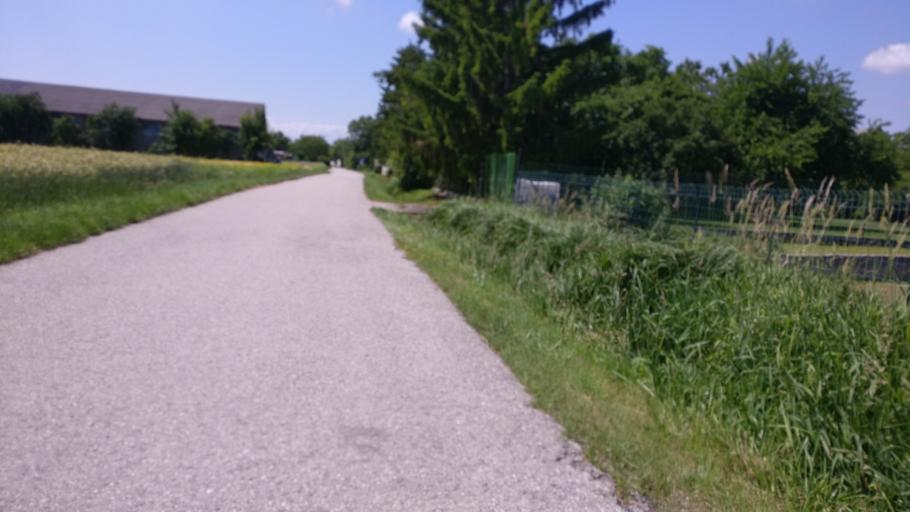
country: AT
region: Lower Austria
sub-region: Politischer Bezirk Baden
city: Schonau an der Triesting
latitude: 47.9363
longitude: 16.2582
